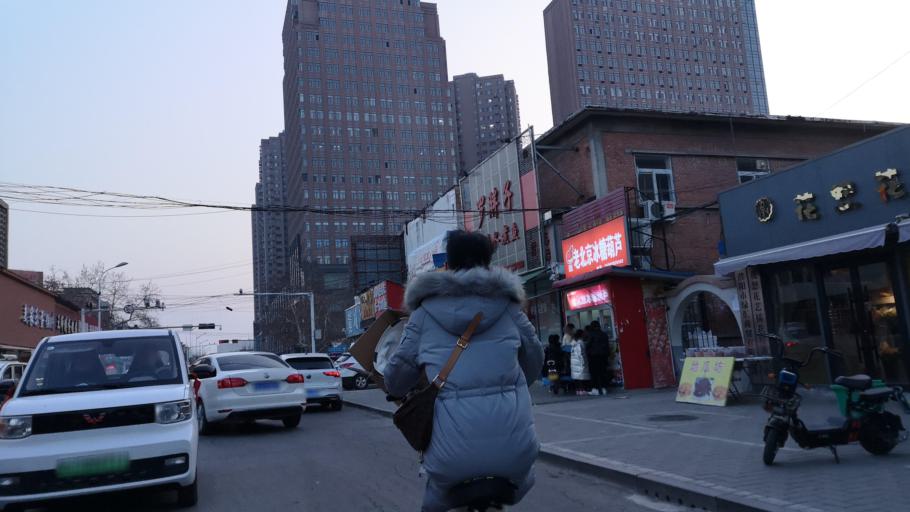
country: CN
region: Henan Sheng
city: Zhongyuanlu
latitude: 35.7760
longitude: 115.0812
